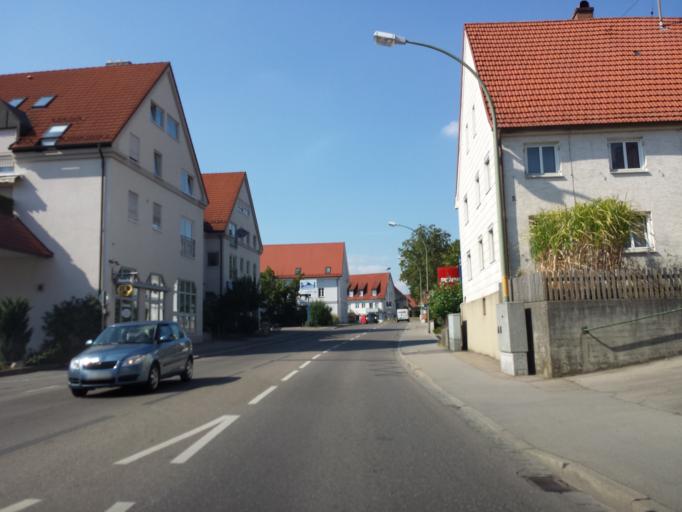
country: DE
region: Bavaria
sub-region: Swabia
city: Krumbach
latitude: 48.2428
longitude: 10.3710
